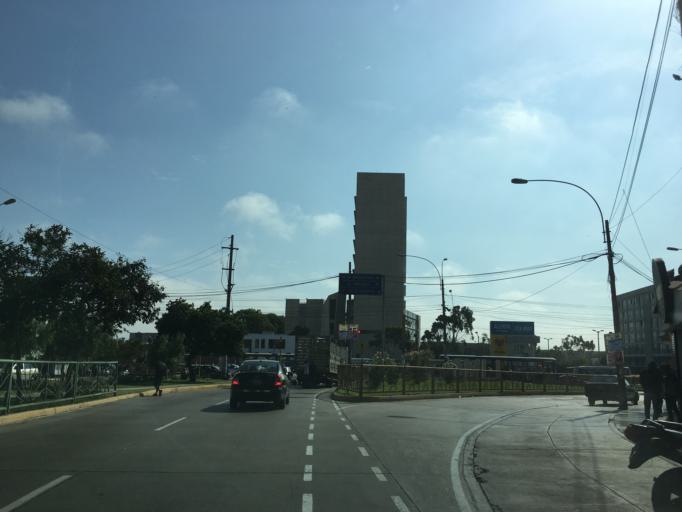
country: PE
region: Callao
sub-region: Callao
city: Callao
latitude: -12.0683
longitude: -77.0771
